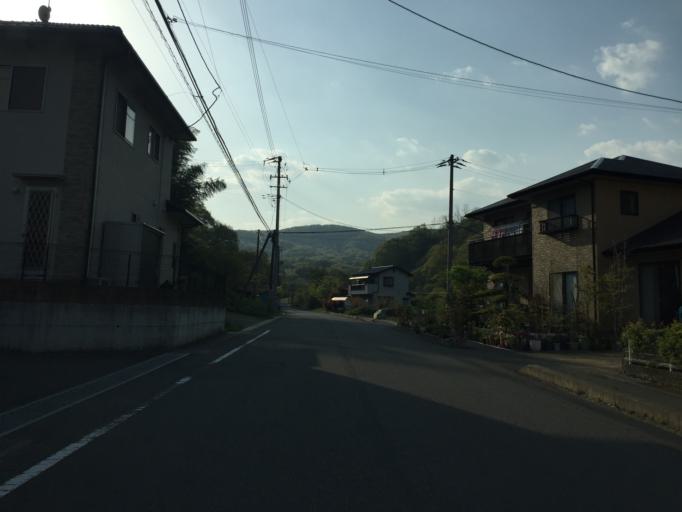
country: JP
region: Fukushima
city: Iwaki
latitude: 37.0465
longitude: 140.8308
